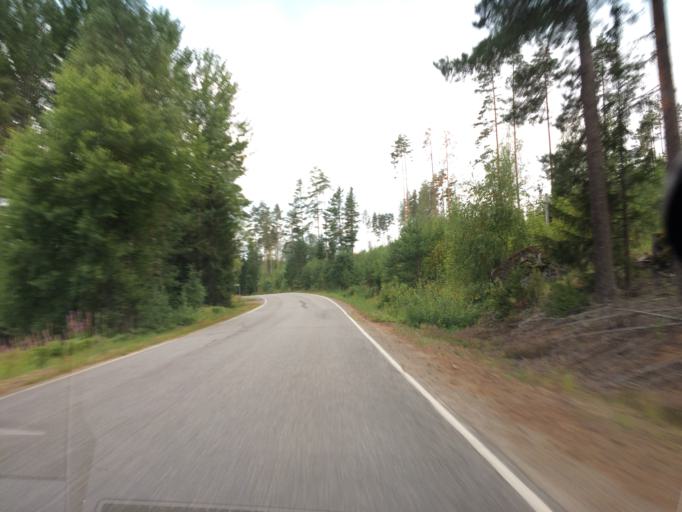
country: FI
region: Pirkanmaa
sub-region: Tampere
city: Luopioinen
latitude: 61.2426
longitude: 24.7090
